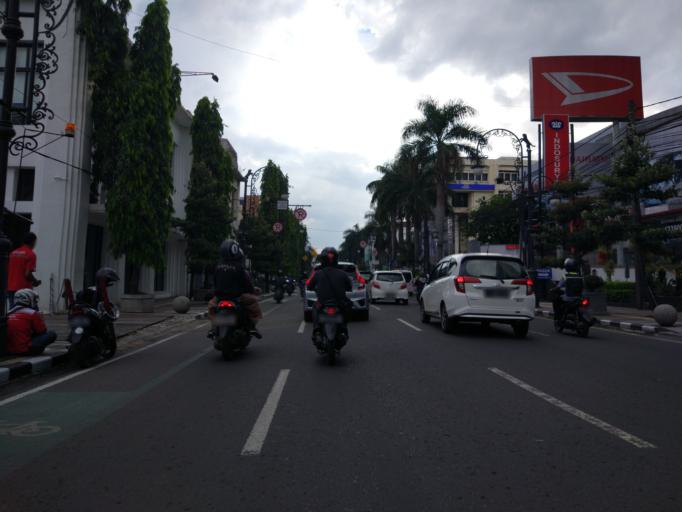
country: ID
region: West Java
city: Bandung
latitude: -6.9222
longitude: 107.6158
